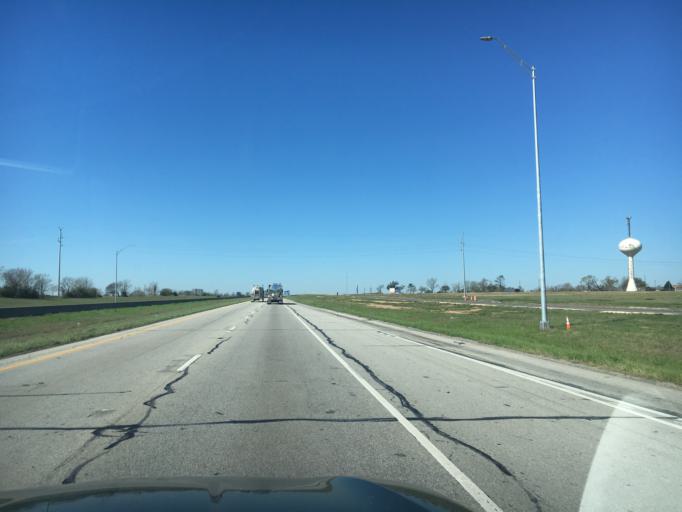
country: US
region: Texas
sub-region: Austin County
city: Sealy
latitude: 29.7622
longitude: -96.1610
